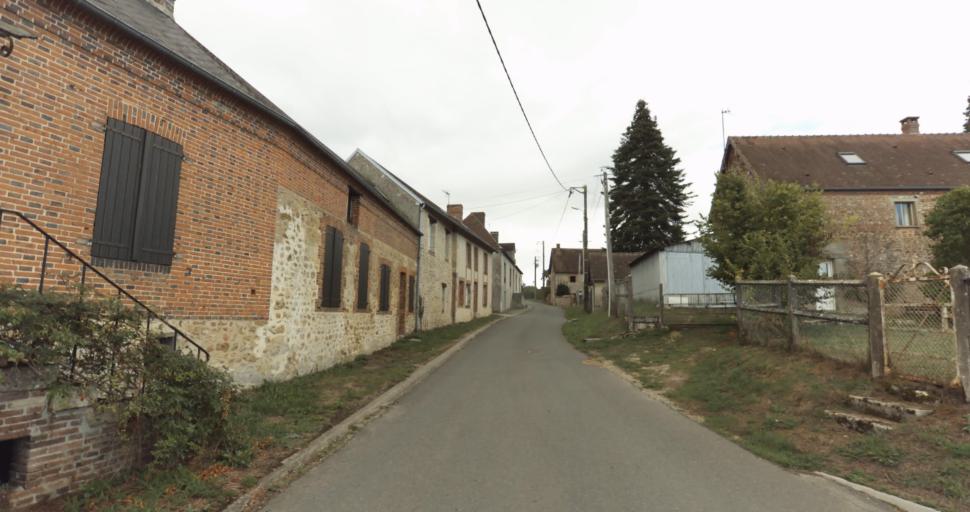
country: FR
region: Lower Normandy
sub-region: Departement de l'Orne
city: Sainte-Gauburge-Sainte-Colombe
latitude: 48.7387
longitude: 0.4059
